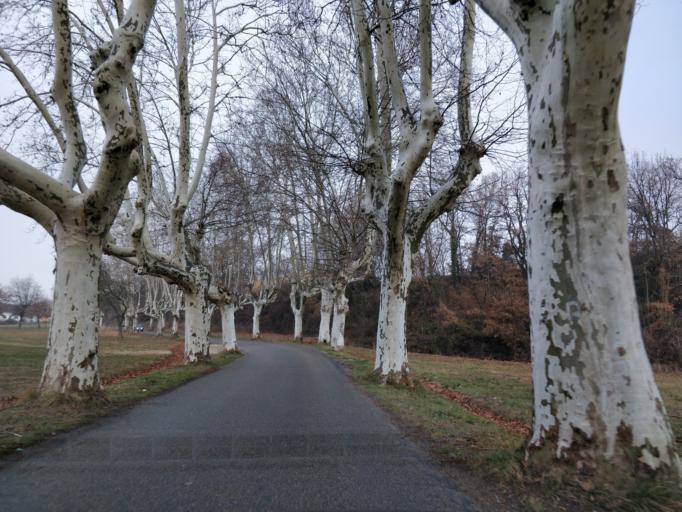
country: FR
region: Languedoc-Roussillon
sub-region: Departement du Gard
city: Saint-Mamert-du-Gard
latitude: 43.8997
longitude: 4.2119
